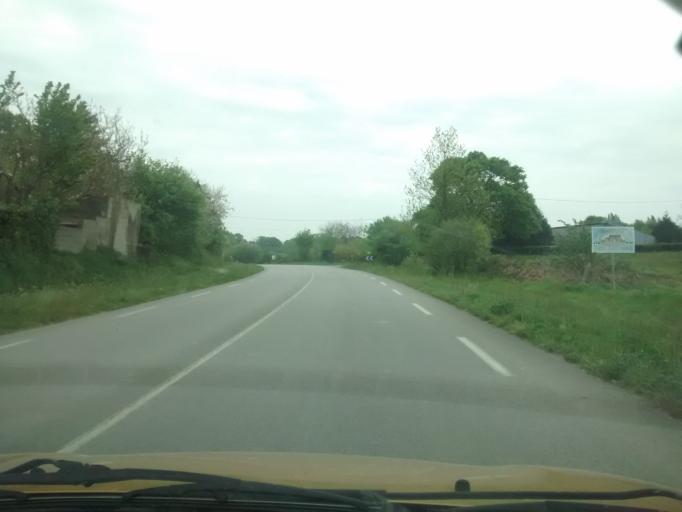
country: FR
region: Brittany
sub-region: Departement du Morbihan
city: Berric
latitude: 47.6180
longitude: -2.5362
